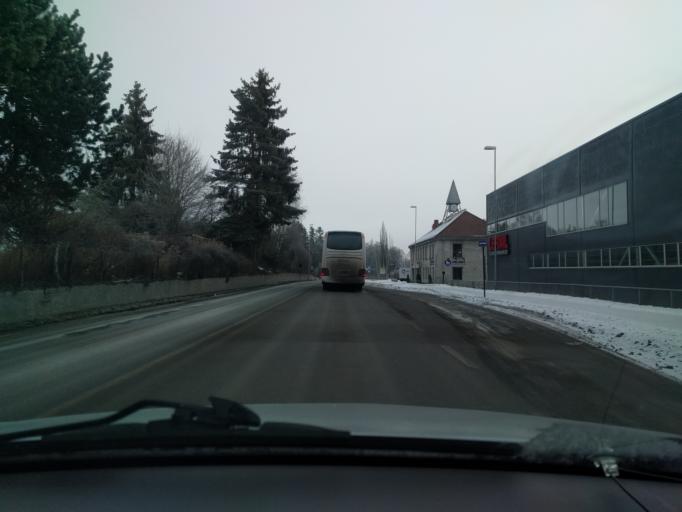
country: NO
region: Hedmark
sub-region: Hamar
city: Hamar
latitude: 60.7970
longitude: 11.0995
